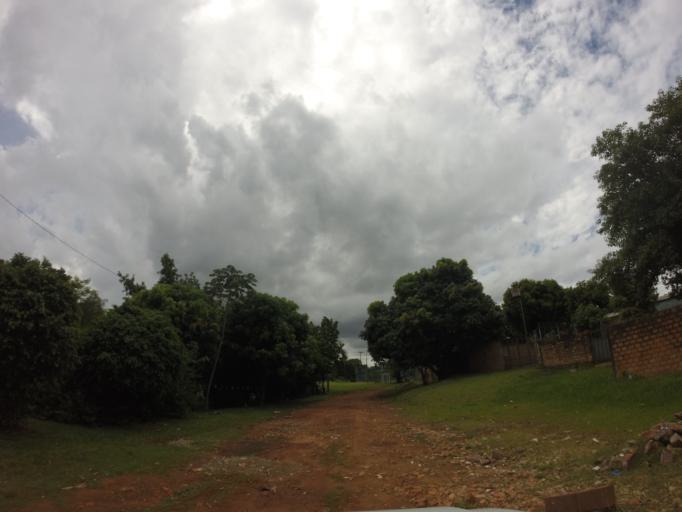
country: PY
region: Alto Parana
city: Ciudad del Este
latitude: -25.4132
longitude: -54.6291
